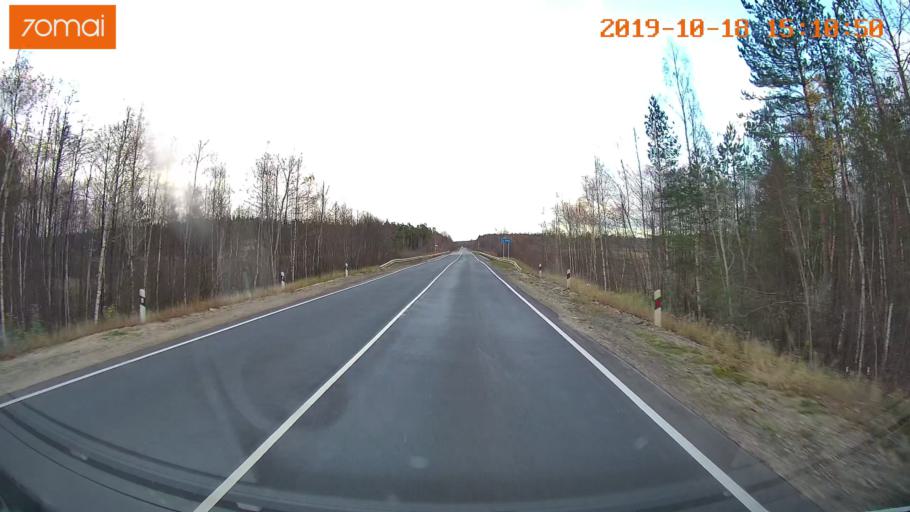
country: RU
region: Vladimir
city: Gus'-Khrustal'nyy
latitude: 55.5693
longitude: 40.6543
